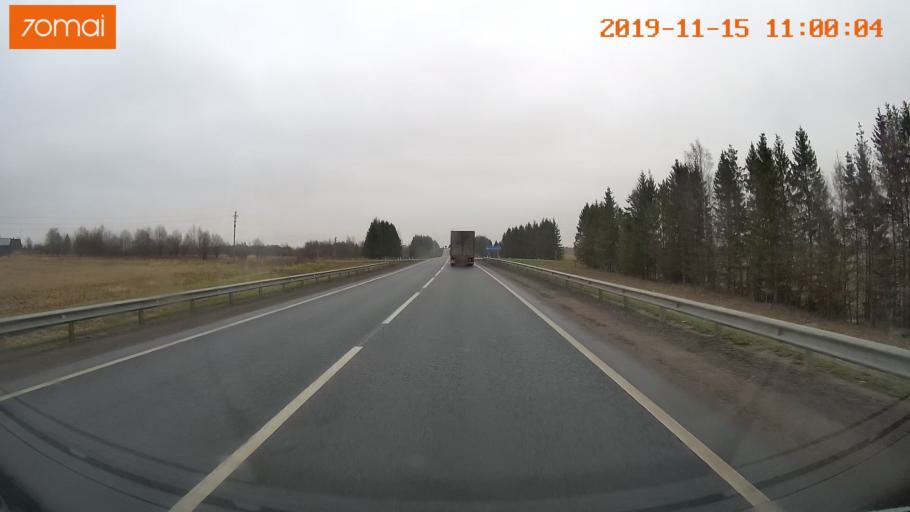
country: RU
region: Vologda
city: Chebsara
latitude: 59.1387
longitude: 38.8909
